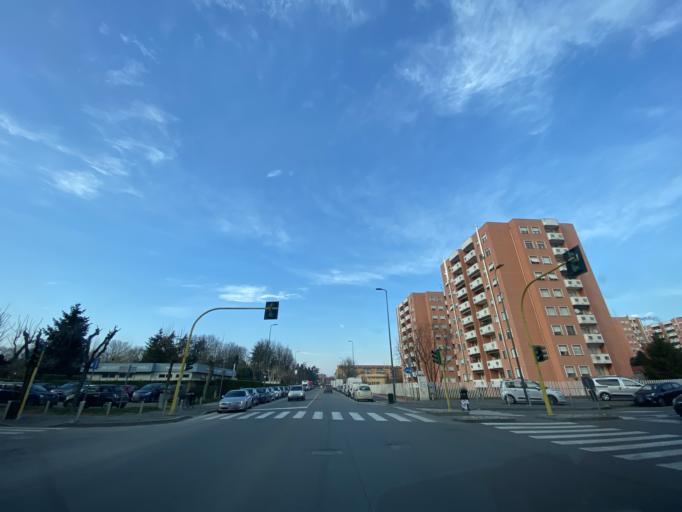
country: IT
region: Lombardy
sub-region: Citta metropolitana di Milano
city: Novate Milanese
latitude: 45.5142
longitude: 9.1365
